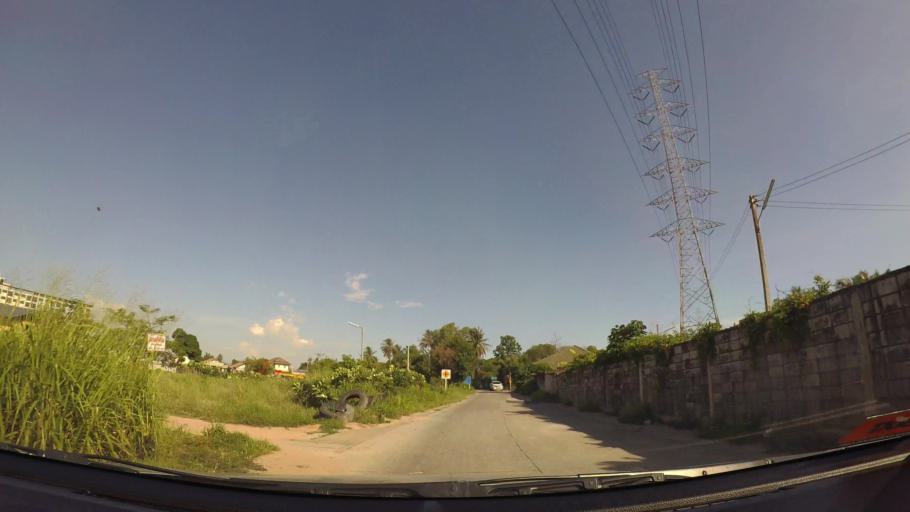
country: TH
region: Chon Buri
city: Si Racha
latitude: 13.1482
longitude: 100.9418
